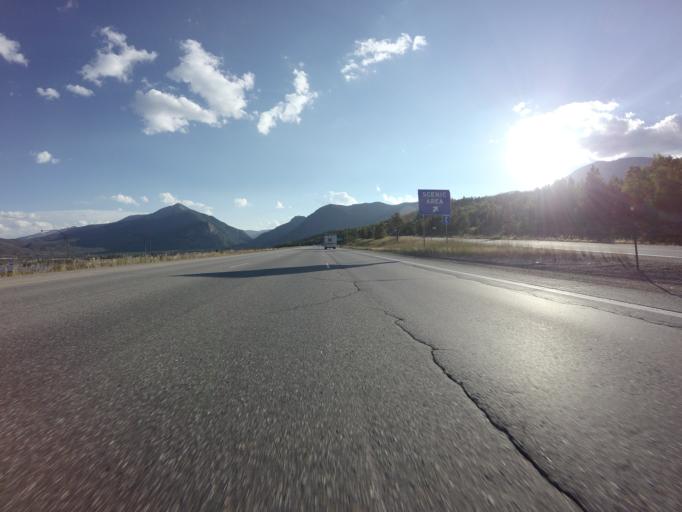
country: US
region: Colorado
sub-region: Summit County
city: Frisco
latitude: 39.6030
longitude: -106.0862
